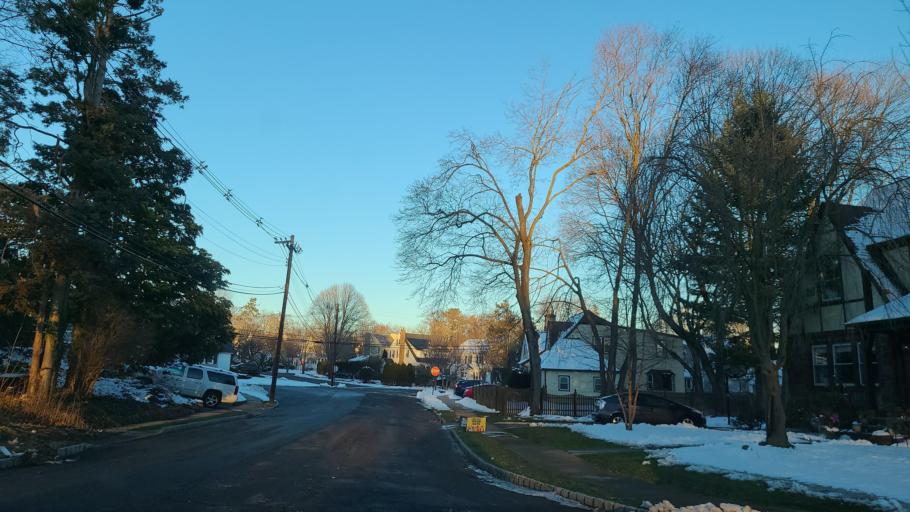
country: US
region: New Jersey
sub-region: Union County
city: Springfield
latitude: 40.7185
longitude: -74.3034
